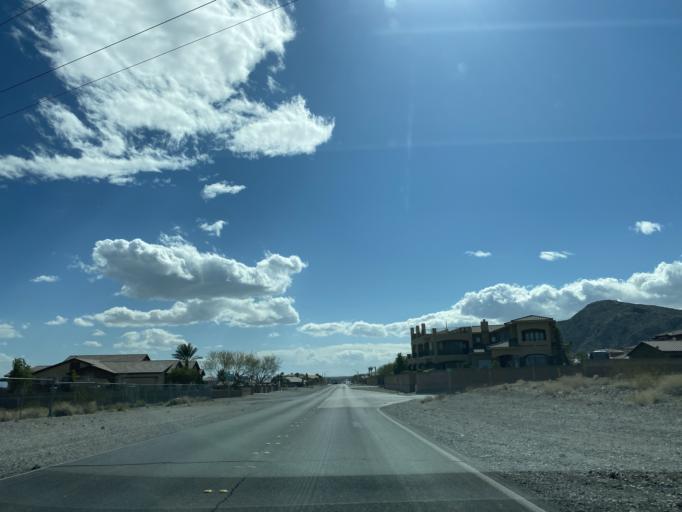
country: US
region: Nevada
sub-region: Clark County
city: Summerlin South
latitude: 36.2525
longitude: -115.3062
